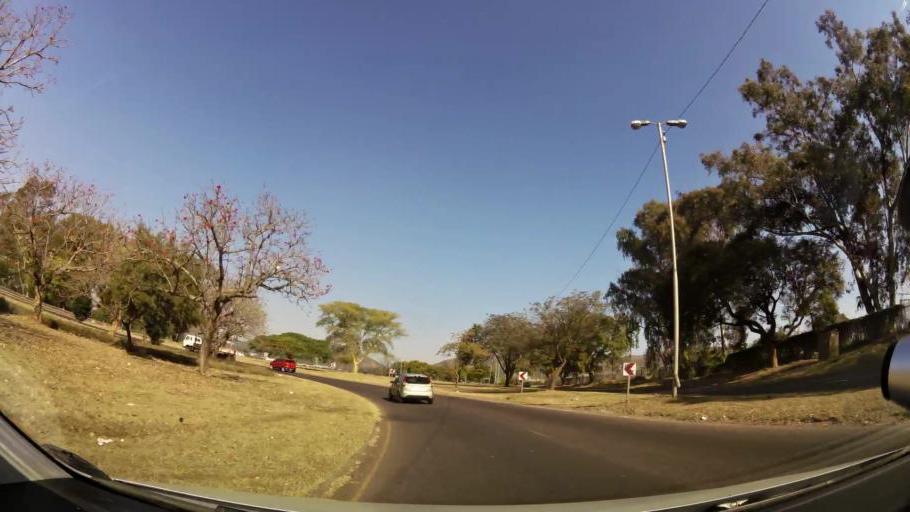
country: ZA
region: Gauteng
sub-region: City of Tshwane Metropolitan Municipality
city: Pretoria
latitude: -25.6677
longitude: 28.1826
